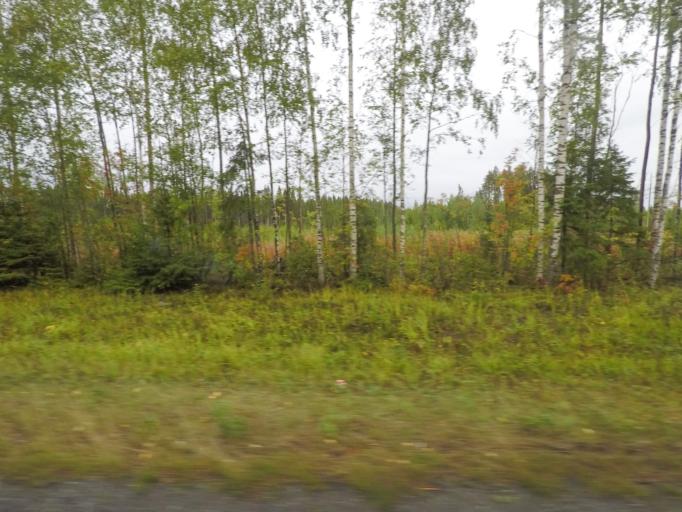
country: FI
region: Southern Savonia
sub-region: Pieksaemaeki
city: Joroinen
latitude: 62.0605
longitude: 27.8090
